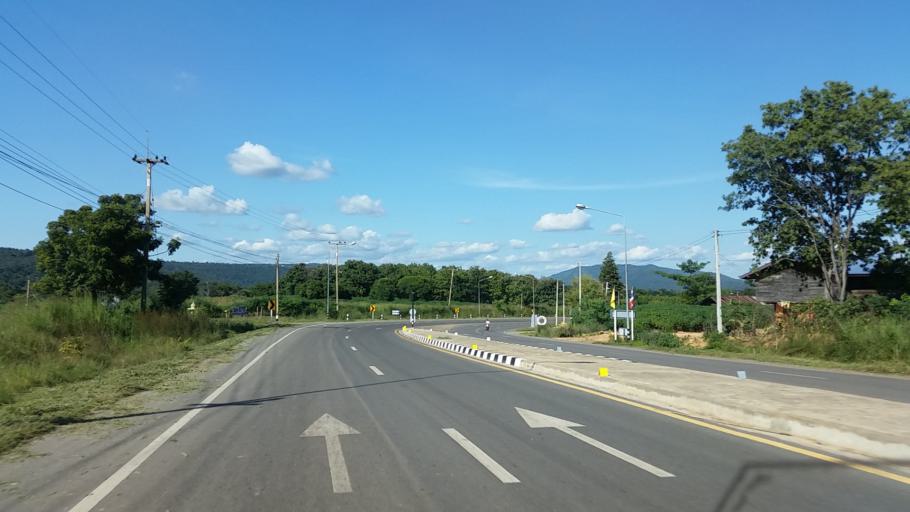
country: TH
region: Chaiyaphum
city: Thep Sathit
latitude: 15.5375
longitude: 101.4310
